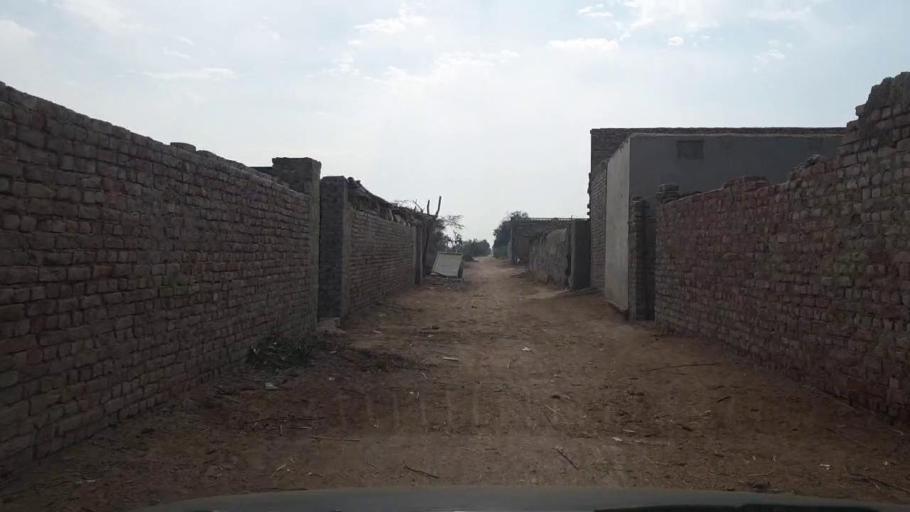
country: PK
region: Sindh
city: Sakrand
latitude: 26.0004
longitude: 68.3886
